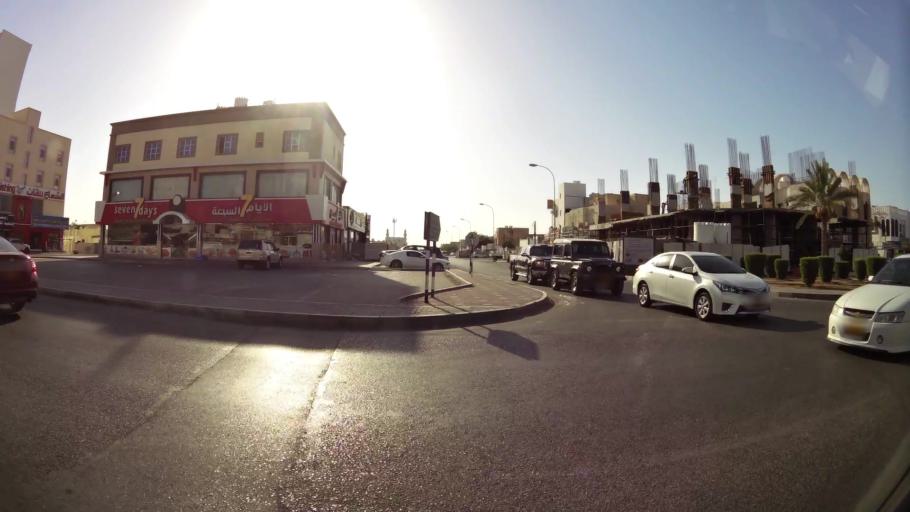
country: OM
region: Muhafazat Masqat
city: As Sib al Jadidah
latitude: 23.6274
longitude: 58.1955
